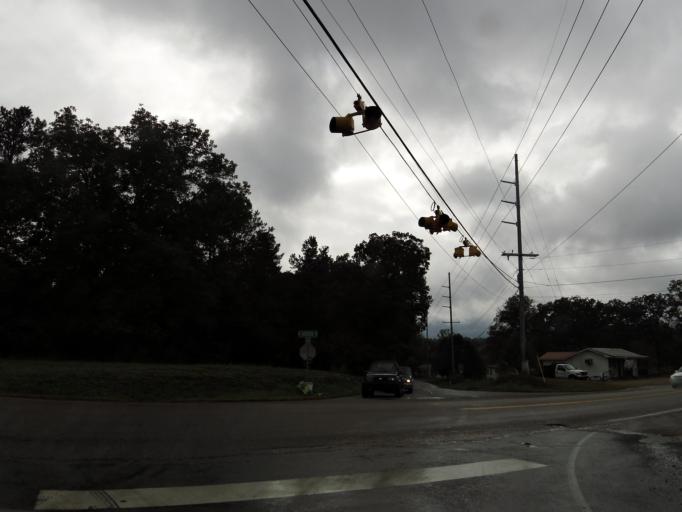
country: US
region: Tennessee
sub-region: Bradley County
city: Cleveland
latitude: 35.1769
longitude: -84.9180
